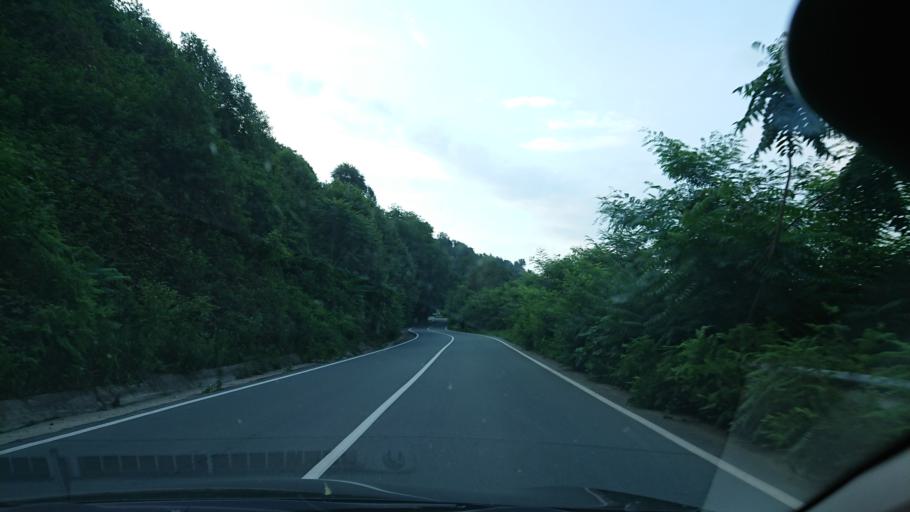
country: TR
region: Rize
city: Cayeli
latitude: 41.0704
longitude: 40.7118
